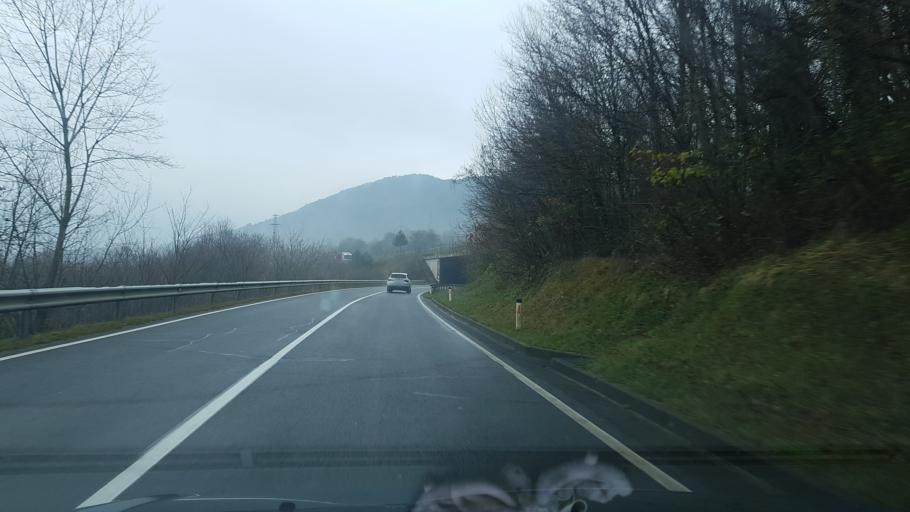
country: SI
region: Sezana
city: Sezana
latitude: 45.7155
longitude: 13.8711
